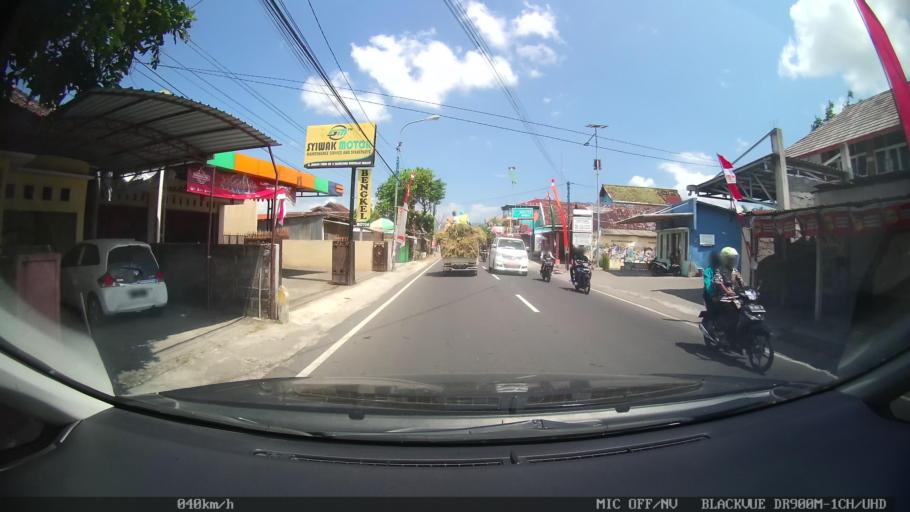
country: ID
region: Daerah Istimewa Yogyakarta
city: Sewon
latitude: -7.9110
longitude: 110.3828
